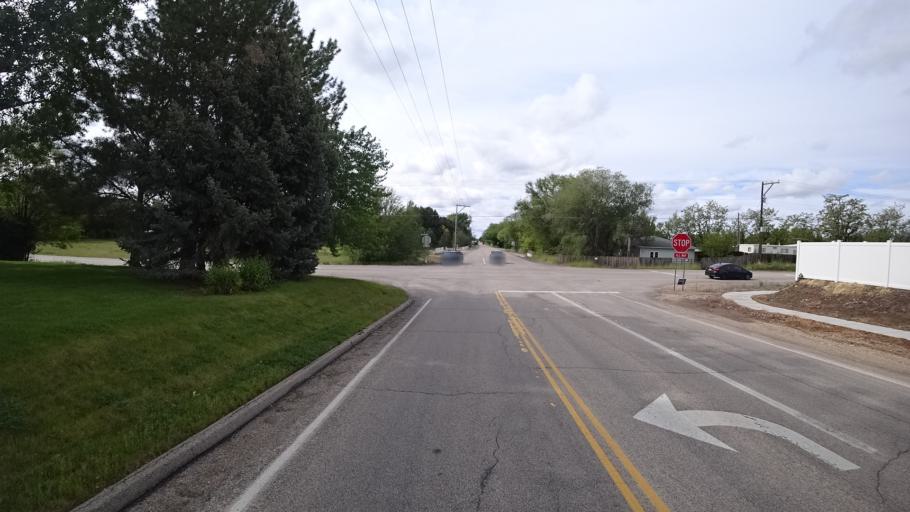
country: US
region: Idaho
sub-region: Ada County
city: Eagle
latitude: 43.7211
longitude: -116.3541
